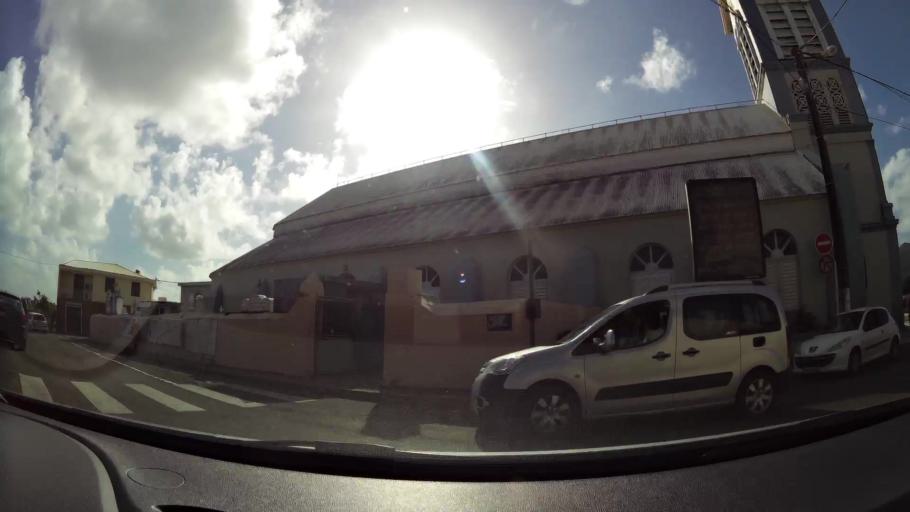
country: MQ
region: Martinique
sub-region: Martinique
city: Le Robert
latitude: 14.6774
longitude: -60.9389
